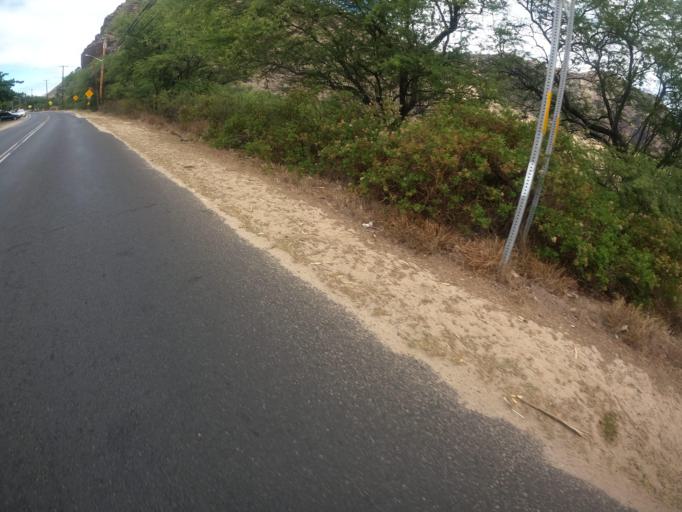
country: US
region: Hawaii
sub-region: Honolulu County
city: Makaha
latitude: 21.4777
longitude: -158.2205
